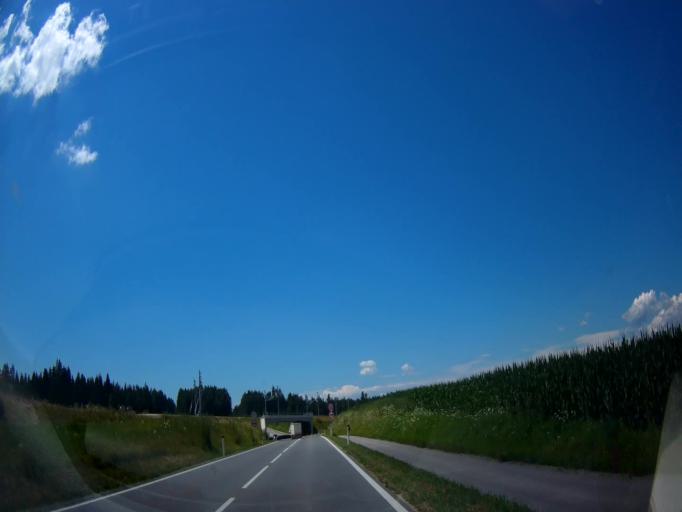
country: AT
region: Carinthia
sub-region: Politischer Bezirk Volkermarkt
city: Eberndorf
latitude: 46.6110
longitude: 14.6756
